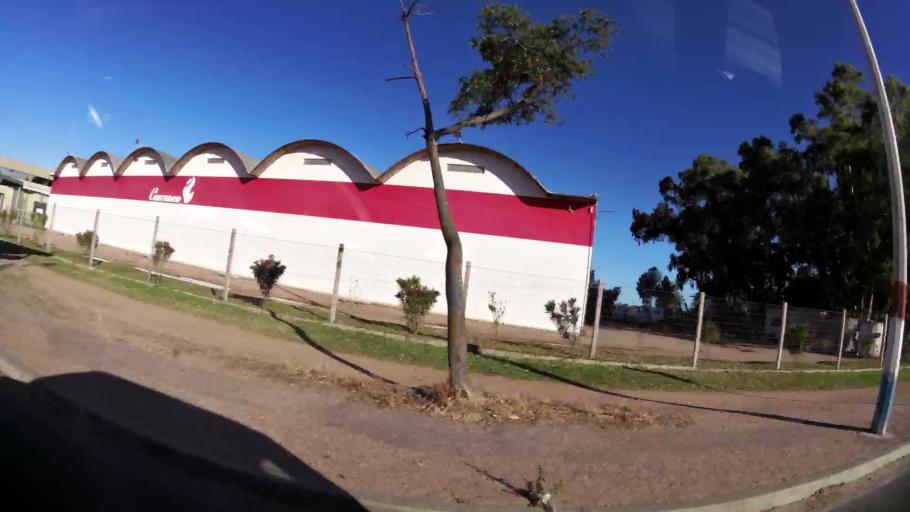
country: UY
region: Canelones
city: Paso de Carrasco
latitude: -34.8652
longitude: -56.0582
